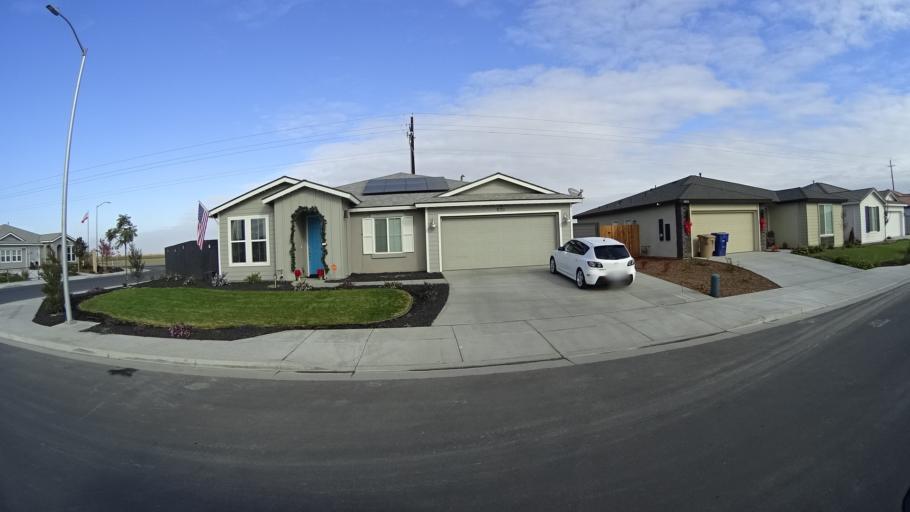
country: US
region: California
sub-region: Kern County
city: Rosedale
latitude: 35.3029
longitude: -119.1436
